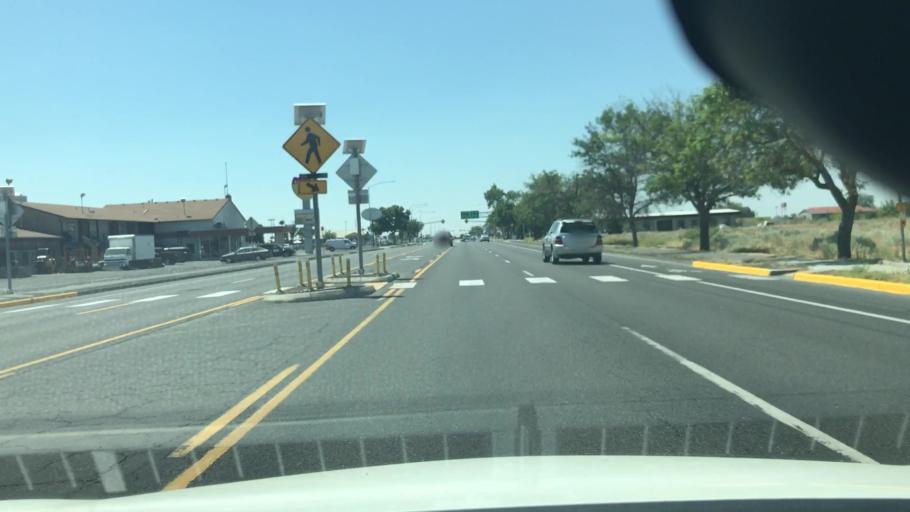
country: US
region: Washington
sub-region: Grant County
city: Cascade Valley
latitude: 47.1044
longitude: -119.3116
